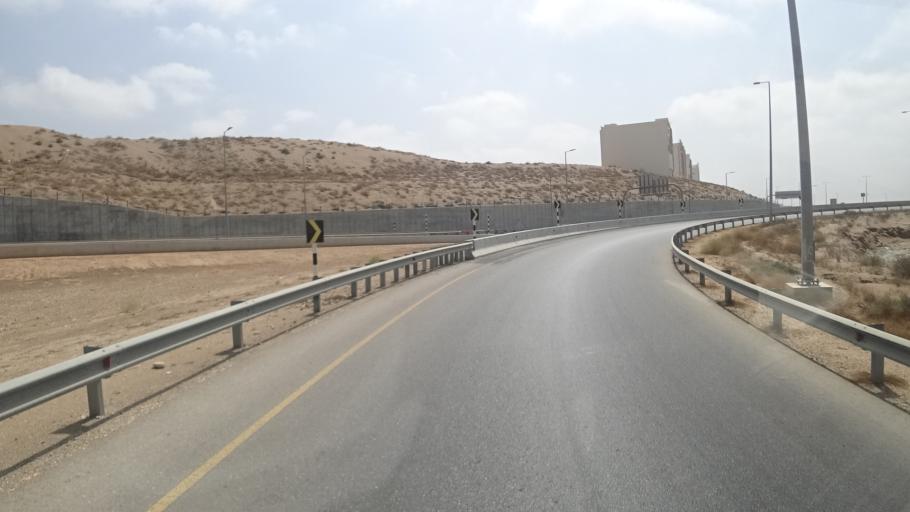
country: OM
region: Muhafazat Masqat
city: Bawshar
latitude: 23.5684
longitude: 58.4088
